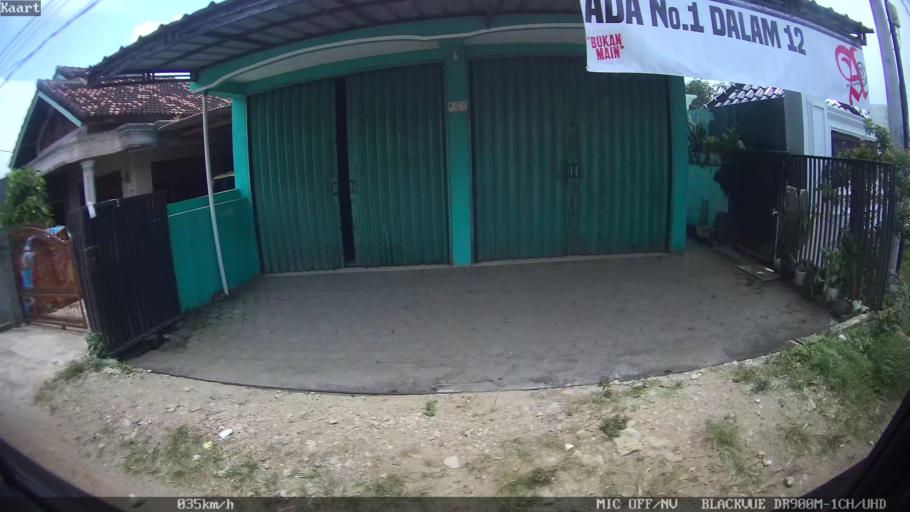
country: ID
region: Lampung
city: Kedaton
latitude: -5.3449
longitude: 105.2432
